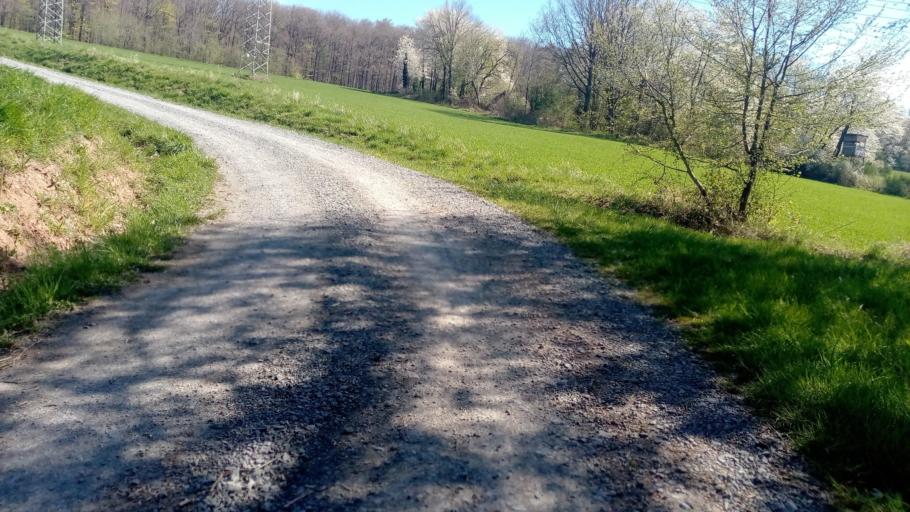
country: DE
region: Bavaria
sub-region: Regierungsbezirk Unterfranken
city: Hasloch
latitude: 49.7970
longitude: 9.5034
